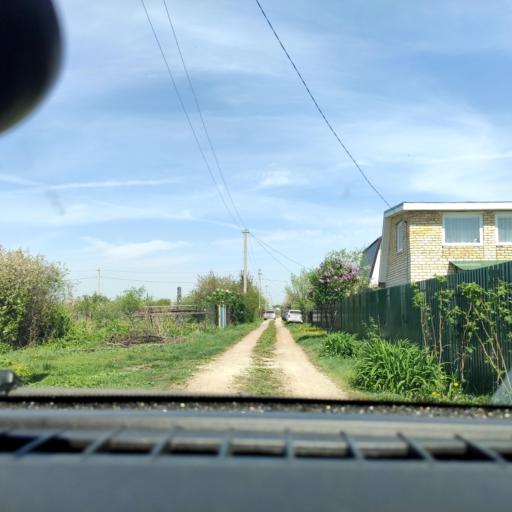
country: RU
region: Samara
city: Tol'yatti
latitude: 53.7068
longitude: 49.4133
